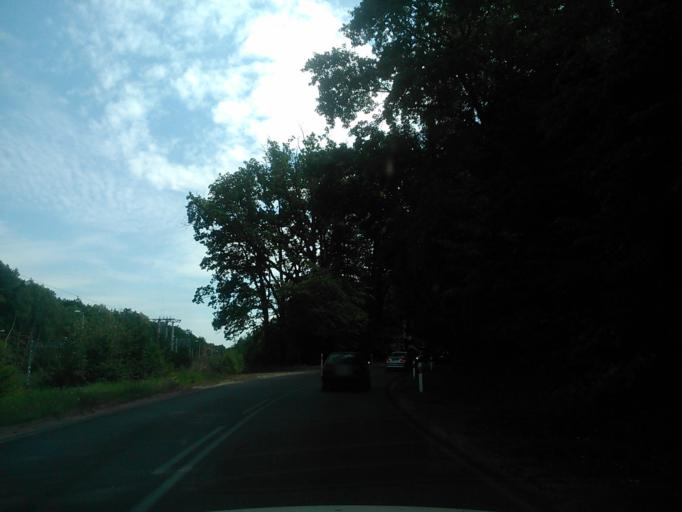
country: PL
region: Warmian-Masurian Voivodeship
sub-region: Powiat dzialdowski
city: Ilowo -Osada
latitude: 53.1593
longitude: 20.3072
